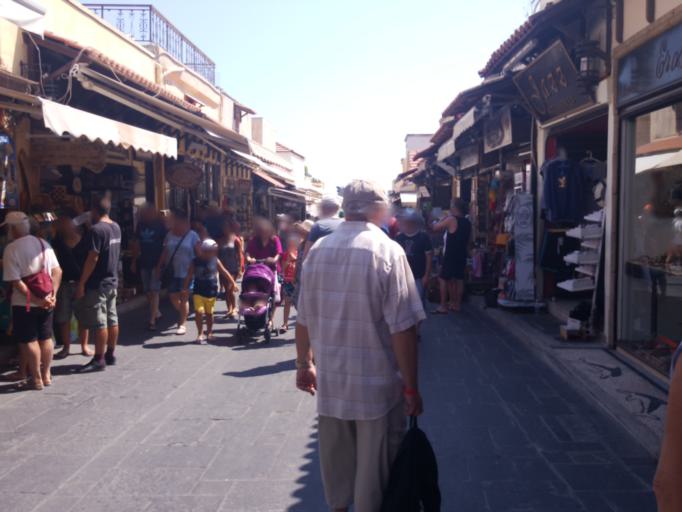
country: GR
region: South Aegean
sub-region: Nomos Dodekanisou
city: Rodos
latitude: 36.4437
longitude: 28.2262
